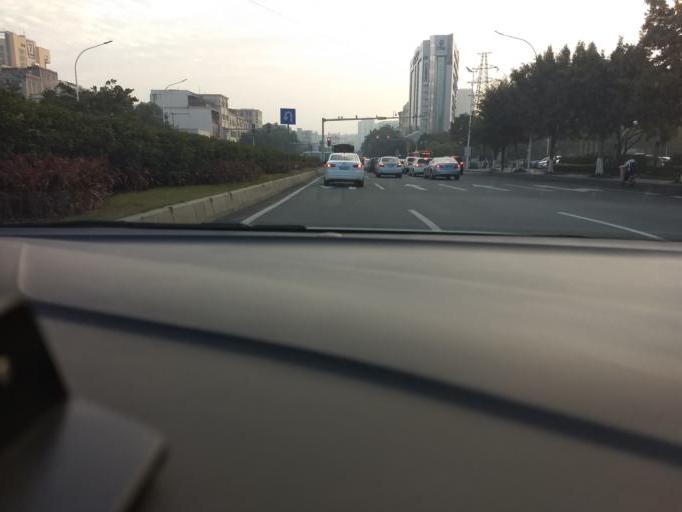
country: CN
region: Guangdong
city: Nansha
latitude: 22.8033
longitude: 113.5400
